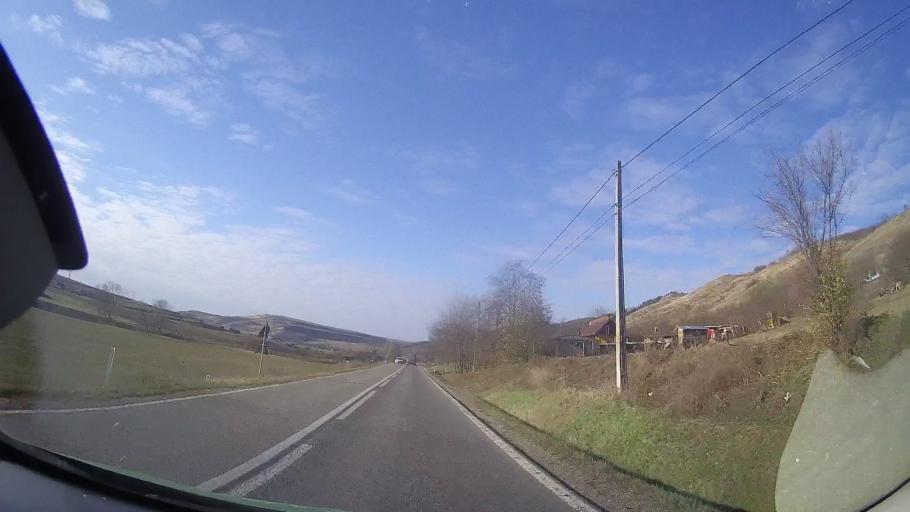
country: RO
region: Cluj
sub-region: Comuna Caianu
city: Vaida-Camaras
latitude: 46.7982
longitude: 23.9484
